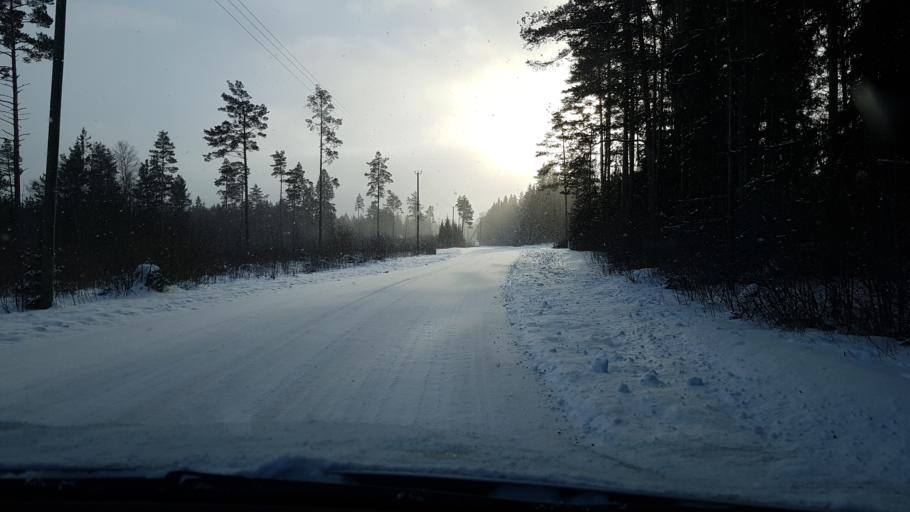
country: EE
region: Harju
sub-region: Nissi vald
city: Turba
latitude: 59.1940
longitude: 24.1401
